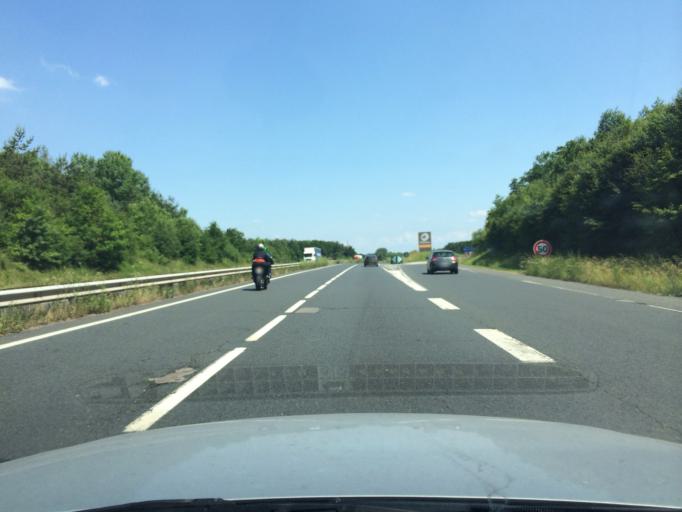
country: FR
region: Lorraine
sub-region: Departement de Meurthe-et-Moselle
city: Damelevieres
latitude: 48.5916
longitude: 6.4150
